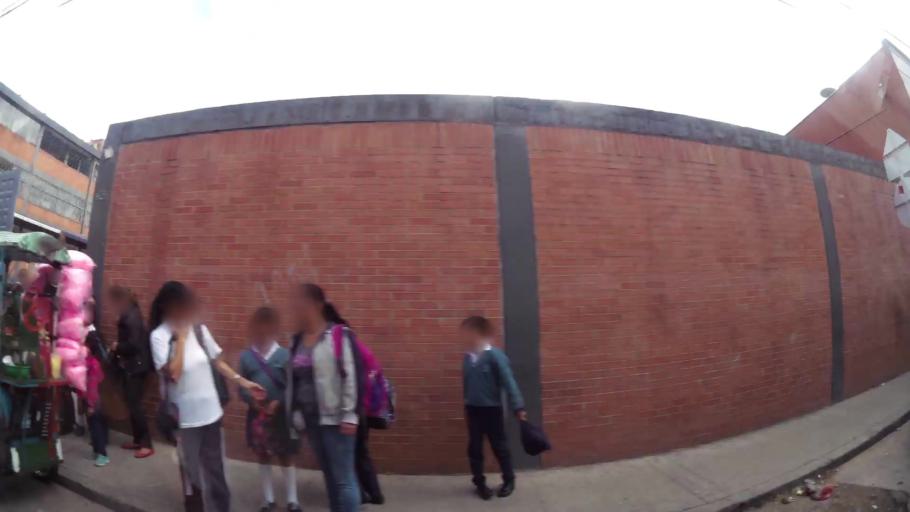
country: CO
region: Cundinamarca
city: Cota
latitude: 4.7258
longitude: -74.0884
